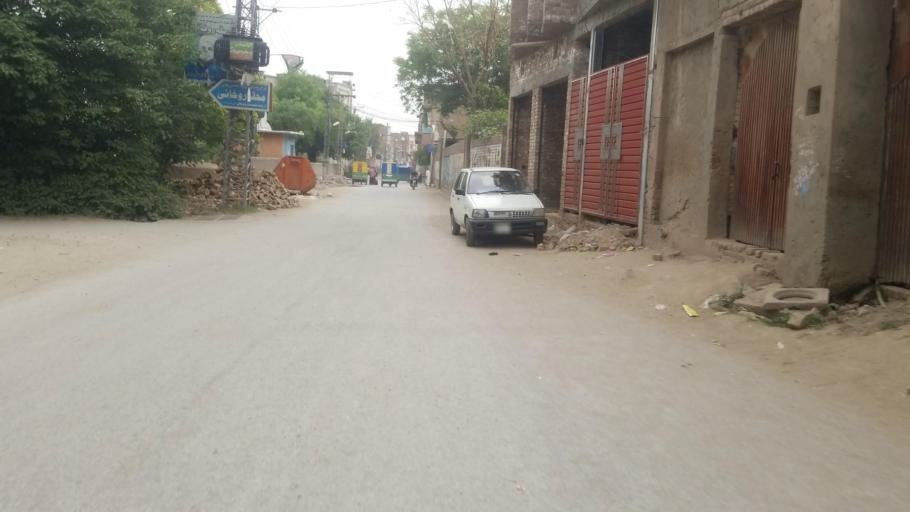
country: PK
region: Khyber Pakhtunkhwa
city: Peshawar
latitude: 33.9916
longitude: 71.5549
